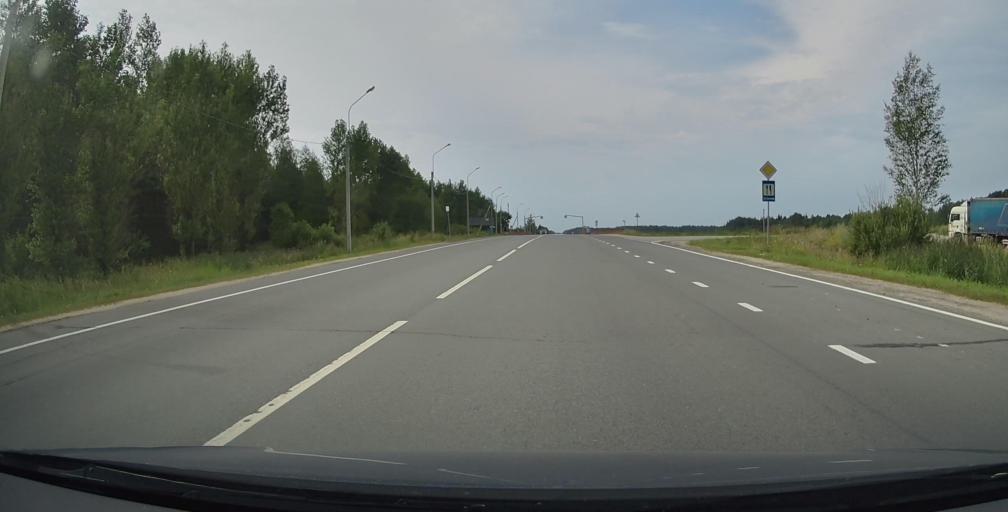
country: RU
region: Jaroslavl
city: Pesochnoye
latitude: 57.9864
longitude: 39.1176
